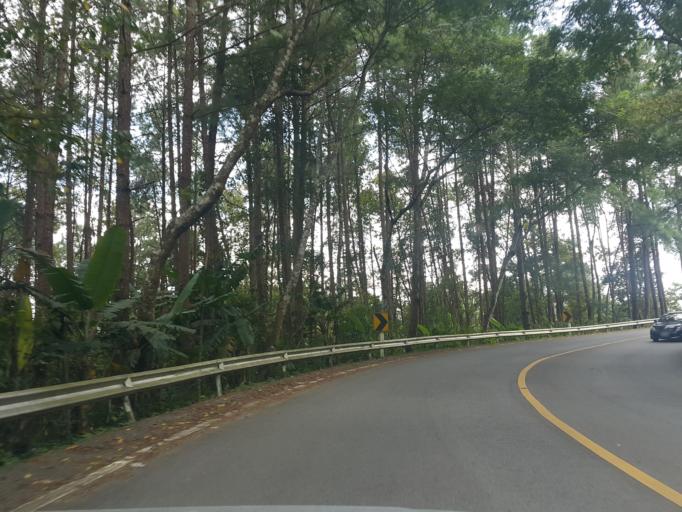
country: TH
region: Chiang Mai
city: Mae Chaem
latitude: 18.5201
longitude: 98.5180
